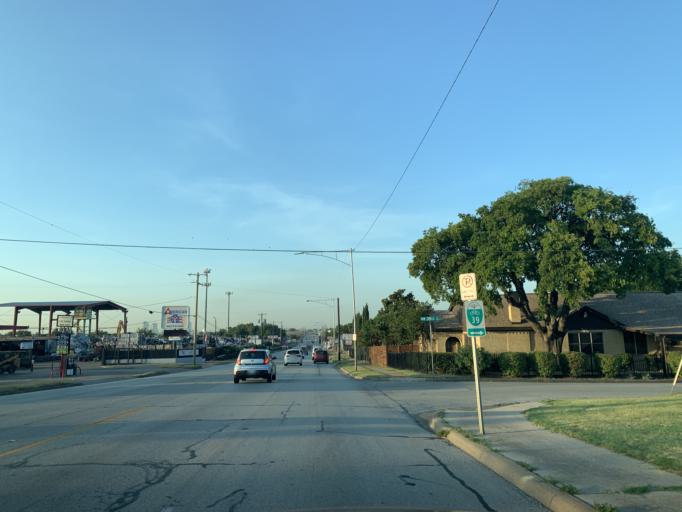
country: US
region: Texas
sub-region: Tarrant County
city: Blue Mound
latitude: 32.8130
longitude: -97.3515
